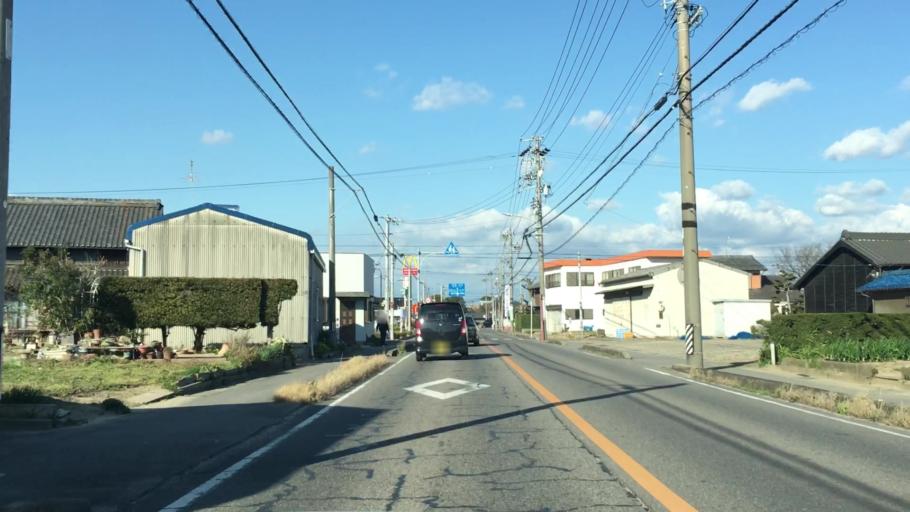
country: JP
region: Aichi
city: Nishio
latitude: 34.8588
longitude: 137.0675
